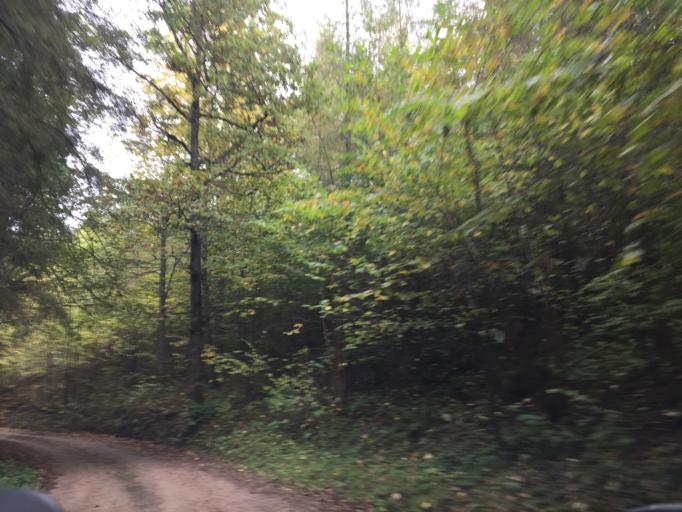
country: LV
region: Auces Novads
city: Auce
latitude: 56.5488
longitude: 23.0411
